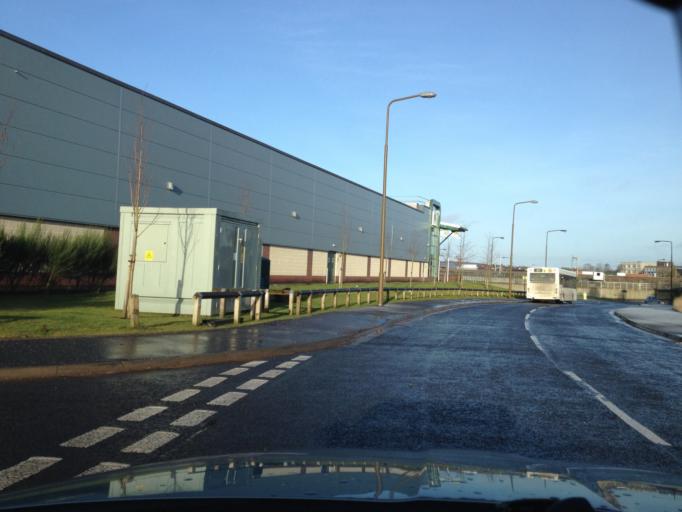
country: GB
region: Scotland
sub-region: West Lothian
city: Bathgate
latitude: 55.8964
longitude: -3.6430
